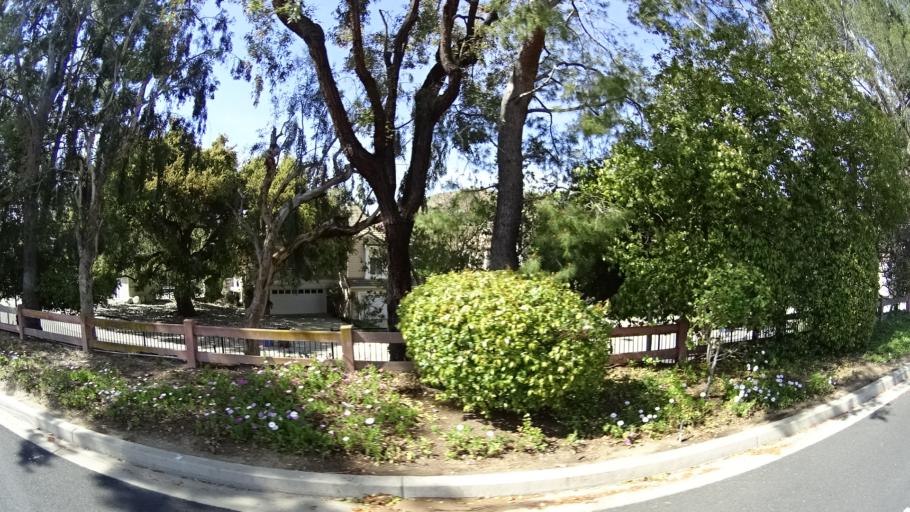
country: US
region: California
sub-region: Ventura County
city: Oak Park
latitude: 34.1862
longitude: -118.7888
